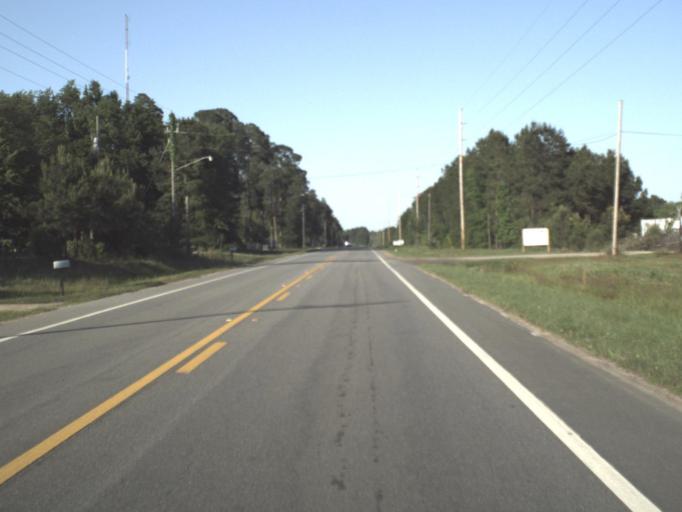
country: US
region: Florida
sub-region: Liberty County
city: Bristol
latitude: 30.3675
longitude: -84.8150
